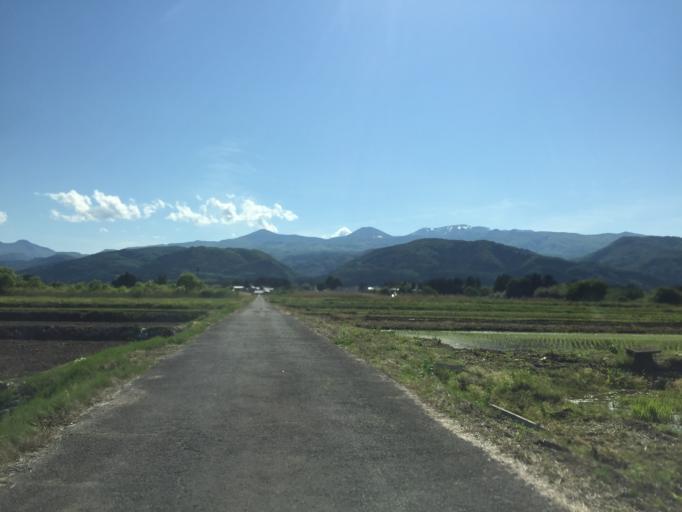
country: JP
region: Fukushima
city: Fukushima-shi
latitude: 37.7477
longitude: 140.3804
